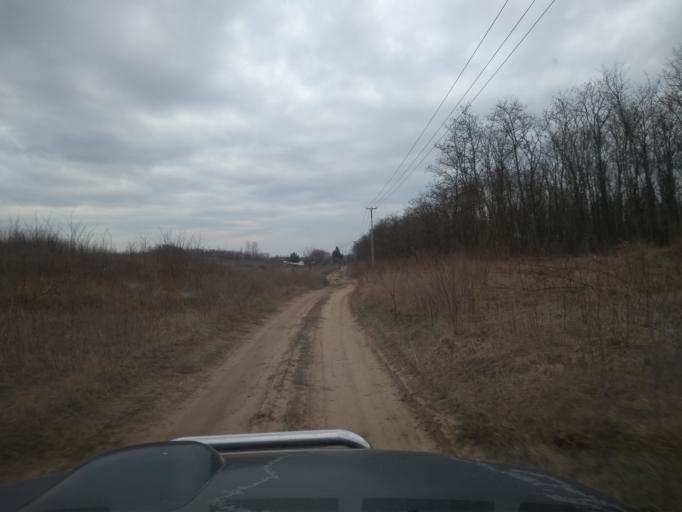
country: HU
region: Szabolcs-Szatmar-Bereg
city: Nyirpazony
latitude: 48.0160
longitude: 21.7886
